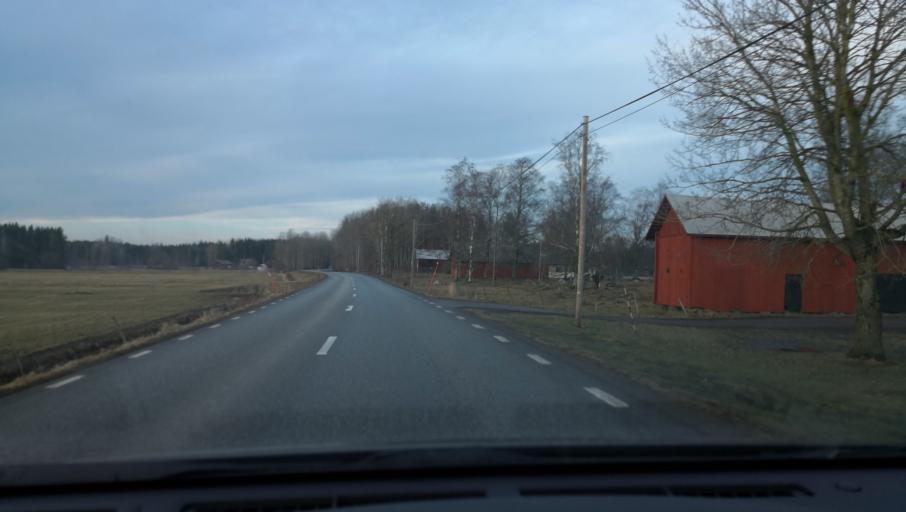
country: SE
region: OErebro
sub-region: Degerfors Kommun
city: Degerfors
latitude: 59.1275
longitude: 14.4100
